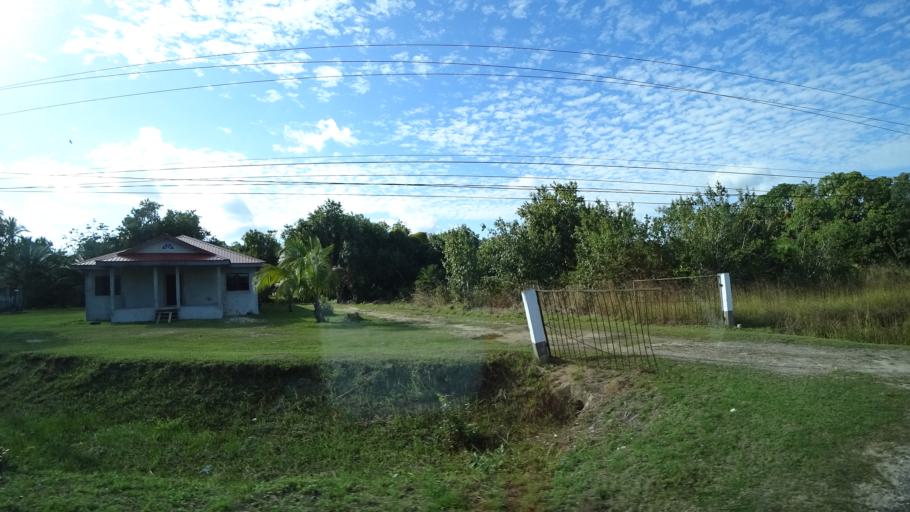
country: BZ
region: Belize
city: Belize City
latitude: 17.5594
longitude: -88.4052
